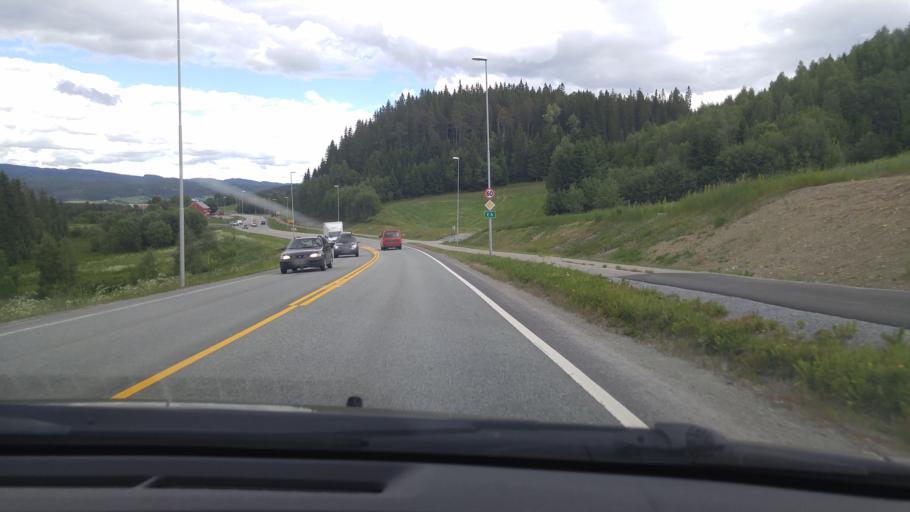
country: NO
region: Nord-Trondelag
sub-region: Steinkjer
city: Steinkjer
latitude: 64.0664
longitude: 11.5079
